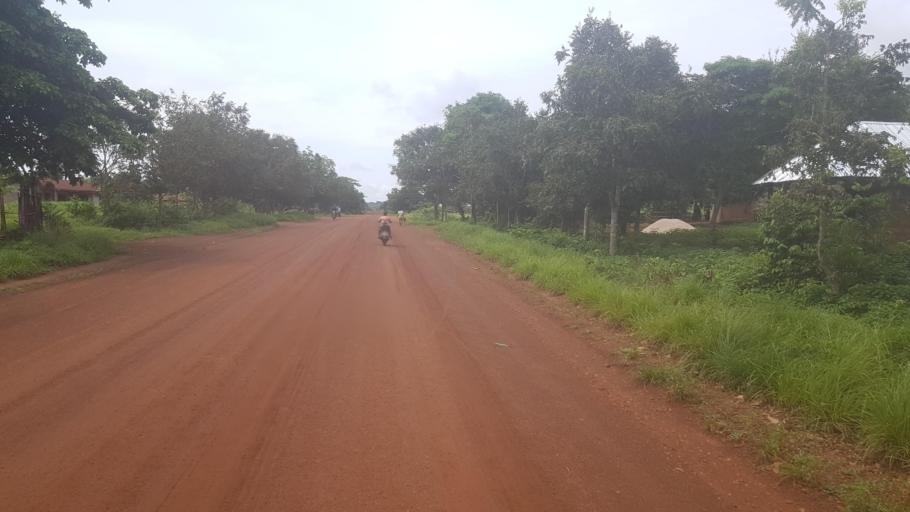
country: SL
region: Southern Province
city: Mogbwemo
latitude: 7.7507
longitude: -12.3070
